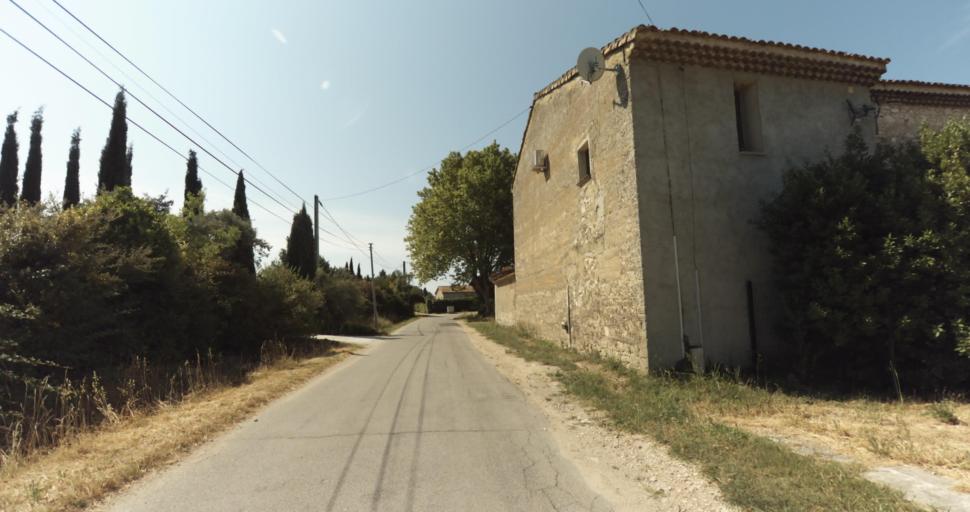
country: FR
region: Provence-Alpes-Cote d'Azur
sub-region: Departement du Vaucluse
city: Monteux
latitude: 44.0164
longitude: 4.9952
